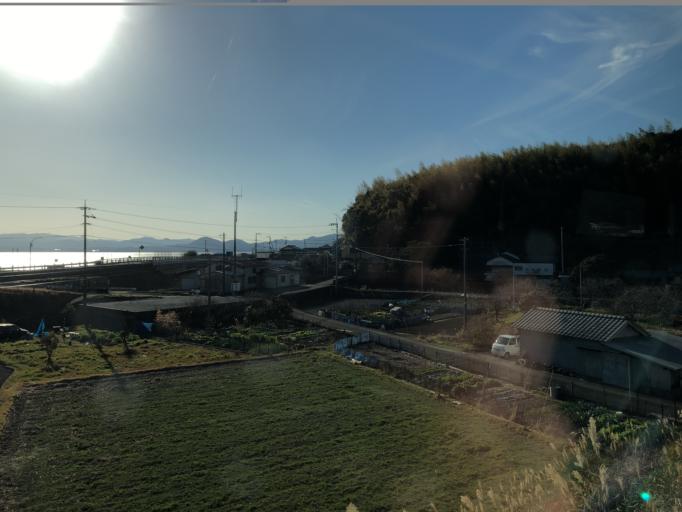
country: JP
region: Kochi
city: Nakamura
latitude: 33.0389
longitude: 133.0712
